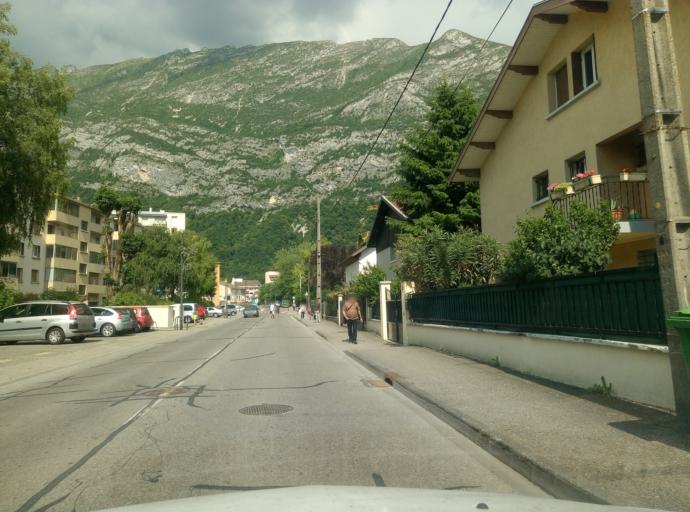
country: FR
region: Rhone-Alpes
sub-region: Departement de l'Isere
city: Saint-Egreve
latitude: 45.2232
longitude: 5.6858
